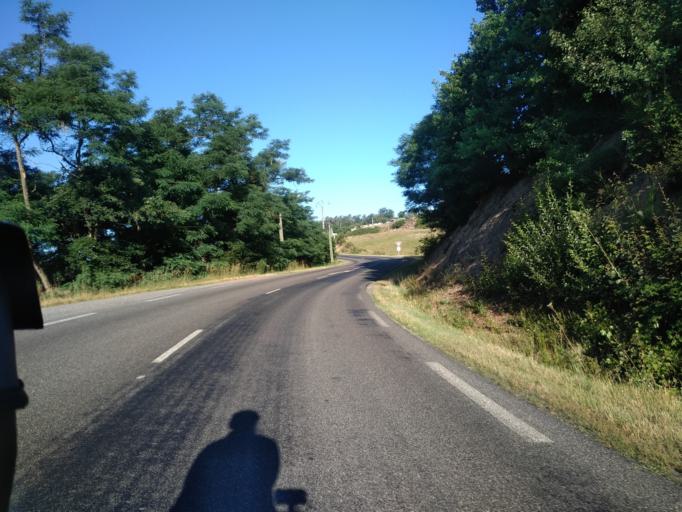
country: FR
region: Rhone-Alpes
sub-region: Departement de la Loire
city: Panissieres
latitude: 45.7514
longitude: 4.3102
